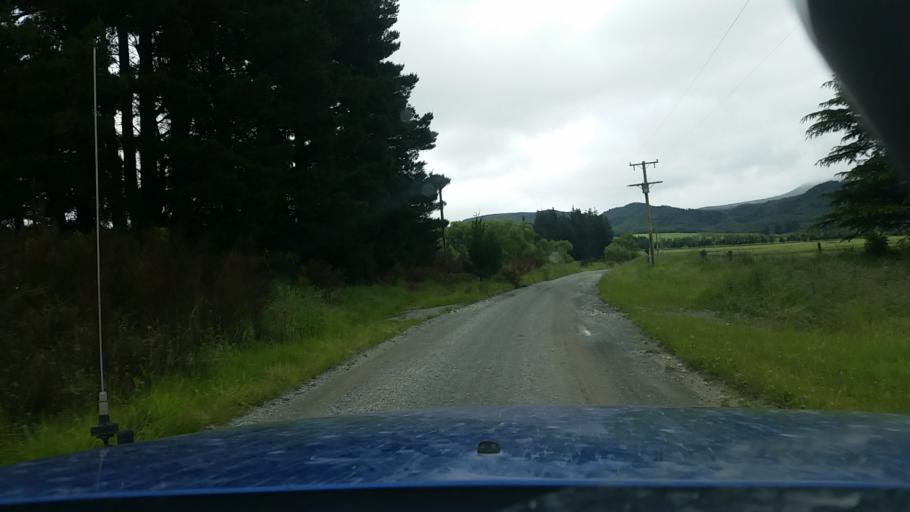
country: NZ
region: Canterbury
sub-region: Ashburton District
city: Methven
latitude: -43.6669
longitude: 171.4279
